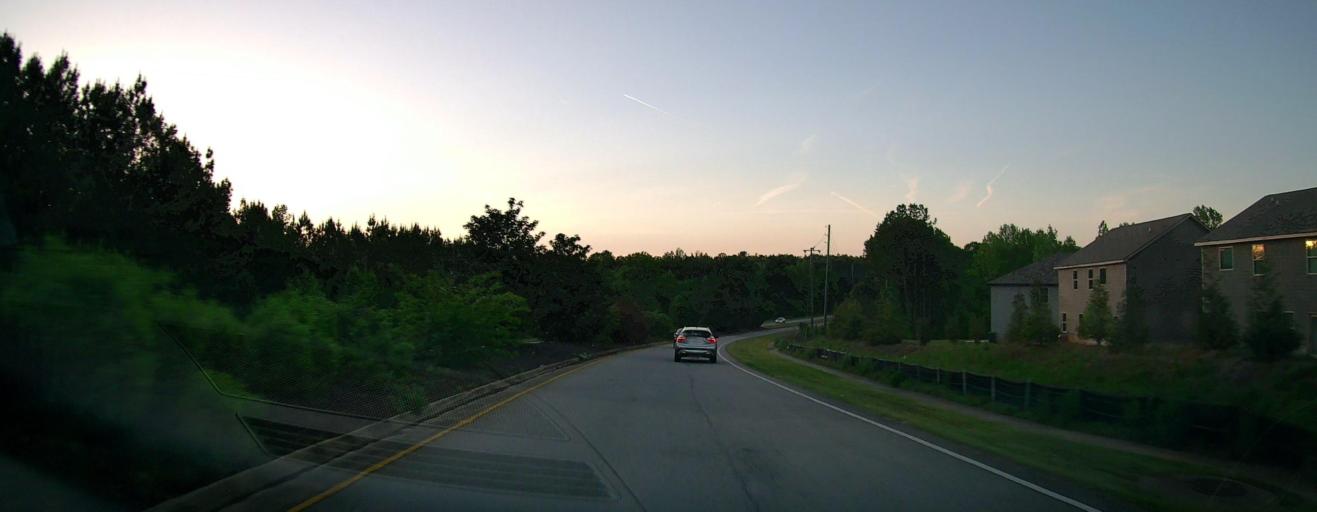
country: US
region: Georgia
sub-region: Henry County
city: McDonough
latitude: 33.4514
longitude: -84.1937
